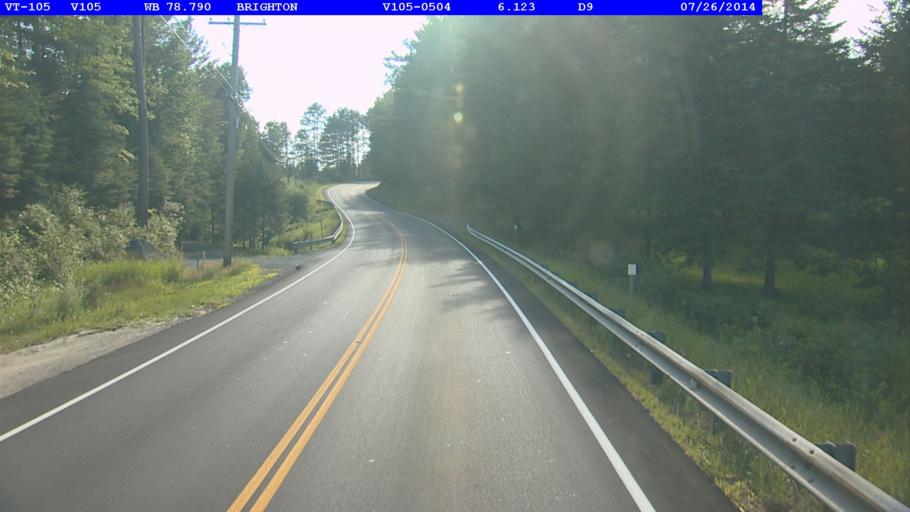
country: US
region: Vermont
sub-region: Caledonia County
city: Lyndonville
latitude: 44.8072
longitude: -71.8533
